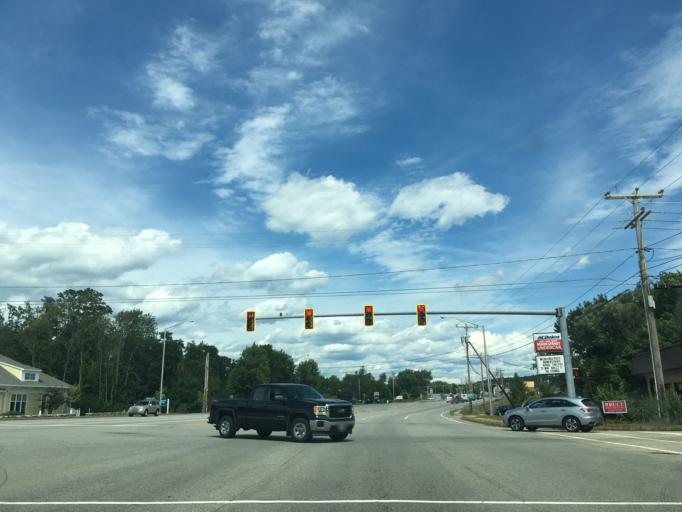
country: US
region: New Hampshire
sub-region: Rockingham County
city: Exeter
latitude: 42.9942
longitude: -70.9258
